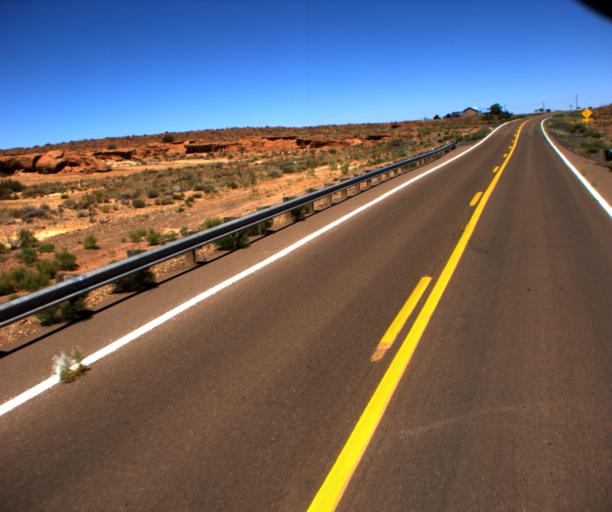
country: US
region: Arizona
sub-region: Navajo County
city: Winslow
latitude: 34.9761
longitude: -110.6540
